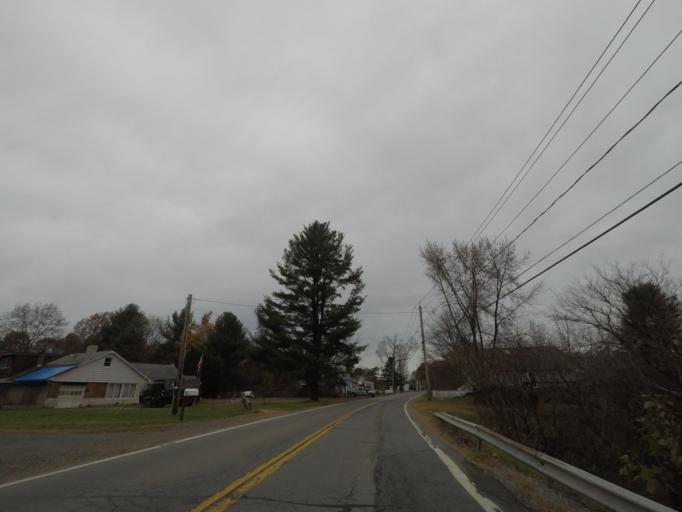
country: US
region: New York
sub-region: Saratoga County
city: Waterford
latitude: 42.8457
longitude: -73.6854
